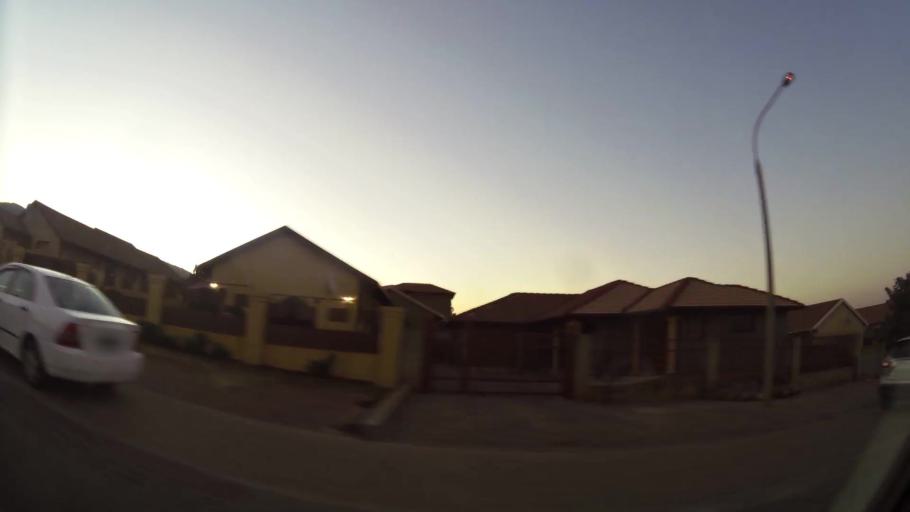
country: ZA
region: North-West
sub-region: Bojanala Platinum District Municipality
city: Rustenburg
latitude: -25.6563
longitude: 27.2083
